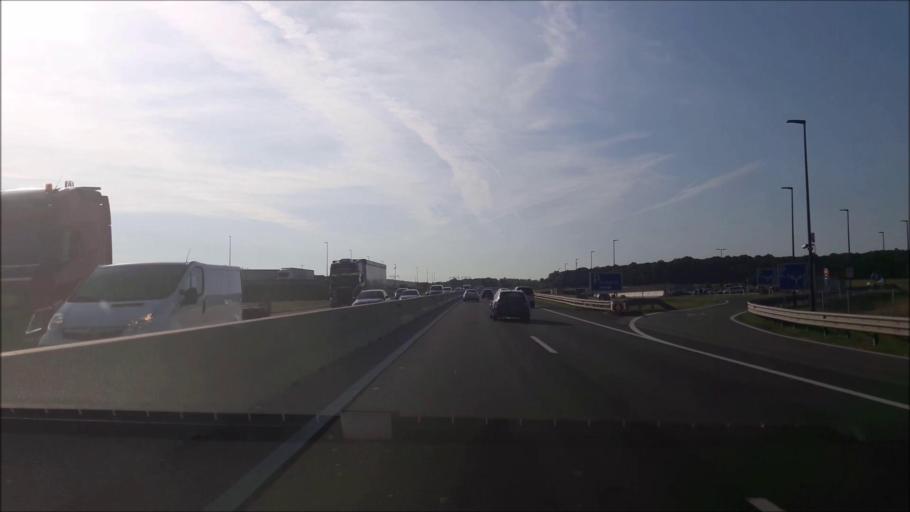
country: AT
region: Lower Austria
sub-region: Politischer Bezirk Wien-Umgebung
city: Fischamend Dorf
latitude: 48.0960
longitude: 16.6582
